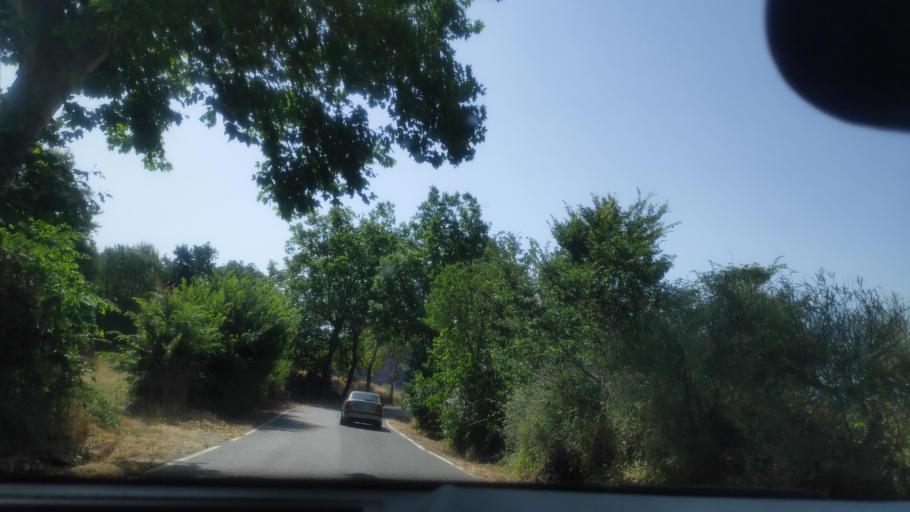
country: ES
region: Andalusia
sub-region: Provincia de Granada
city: Busquistar
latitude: 36.9371
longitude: -3.3024
